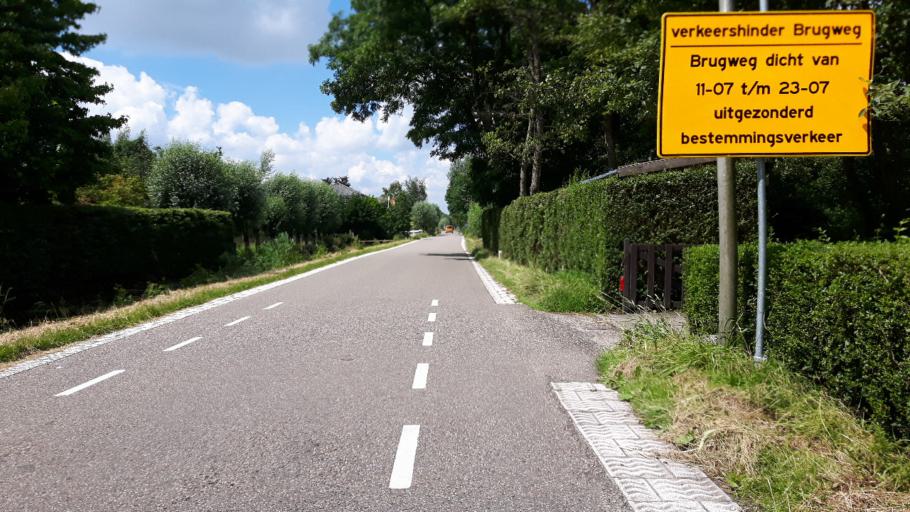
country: NL
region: South Holland
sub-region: Gemeente Gouda
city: Bloemendaal
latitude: 52.0440
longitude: 4.6771
